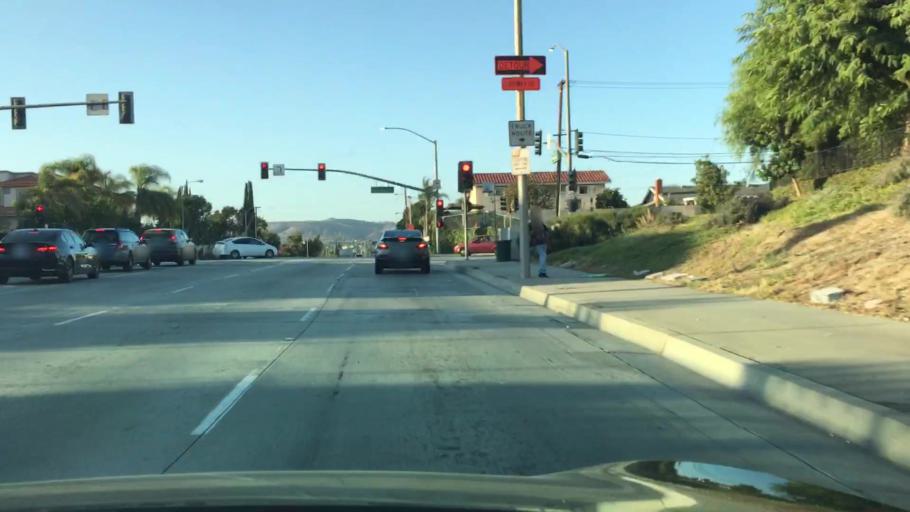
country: US
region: California
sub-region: Los Angeles County
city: South San Jose Hills
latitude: 34.0038
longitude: -117.8875
